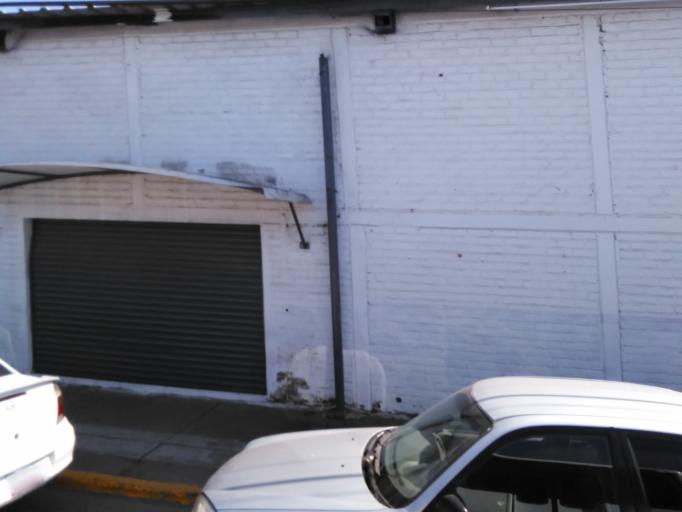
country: MX
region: Nayarit
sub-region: Tepic
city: La Corregidora
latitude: 21.4746
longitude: -104.8530
